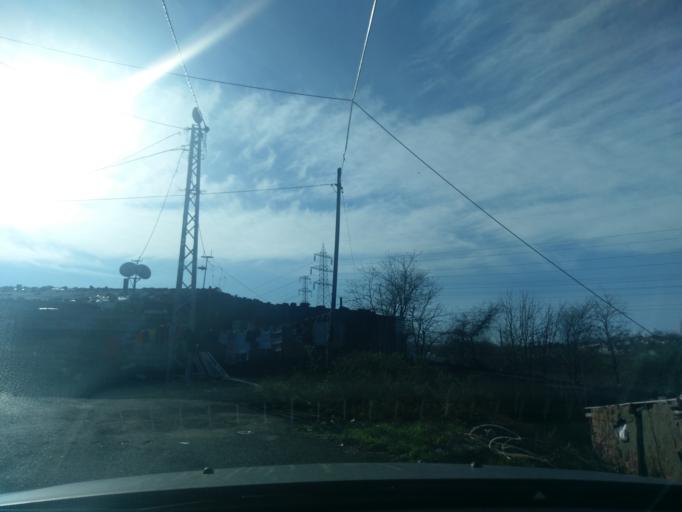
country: TR
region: Istanbul
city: Sultangazi
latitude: 41.1407
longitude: 28.8489
